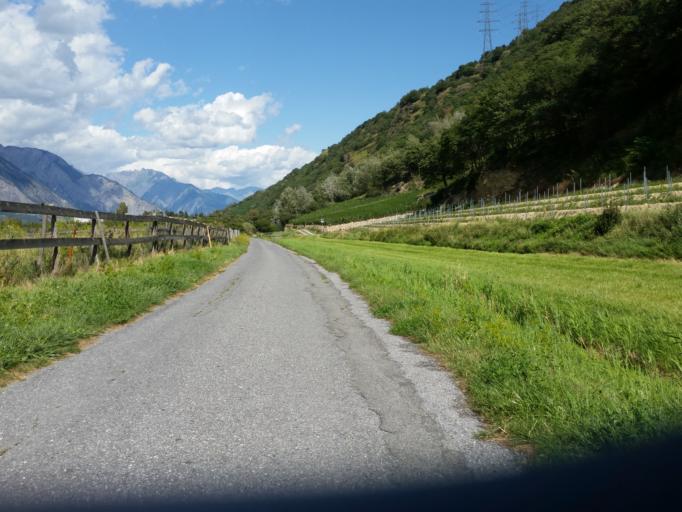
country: CH
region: Valais
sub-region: Martigny District
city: Charrat-les-Chenes
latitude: 46.1345
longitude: 7.1535
